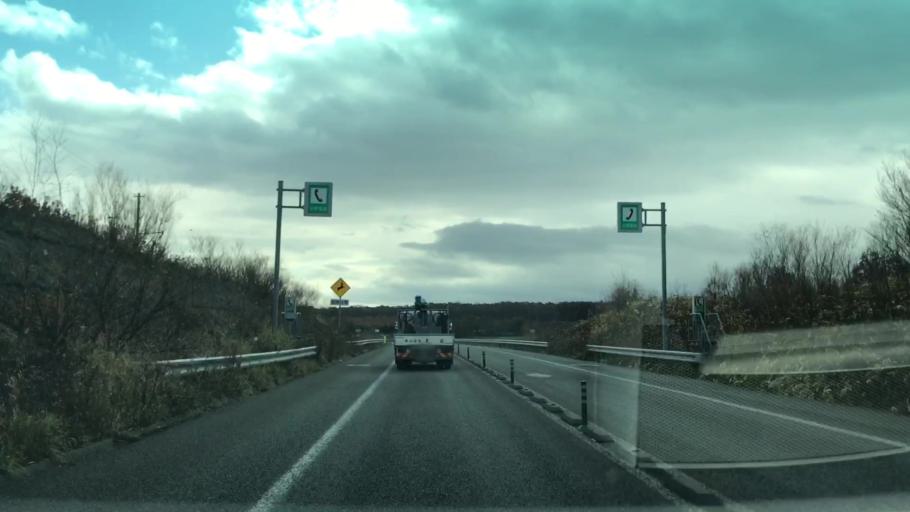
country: JP
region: Hokkaido
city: Tomakomai
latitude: 42.5501
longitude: 141.9929
